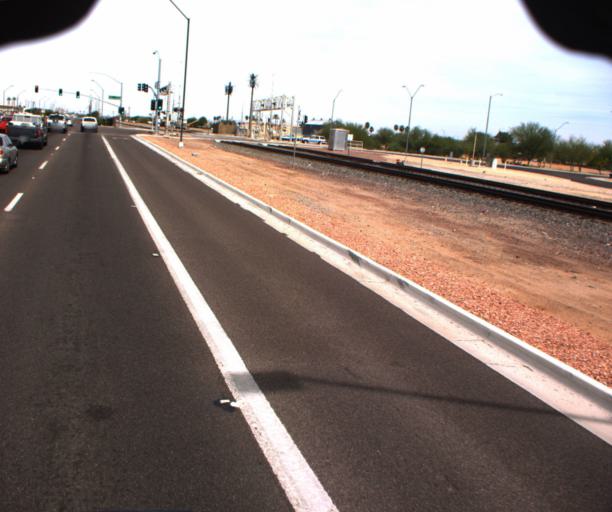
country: US
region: Arizona
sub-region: Maricopa County
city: Peoria
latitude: 33.5772
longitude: -112.2325
